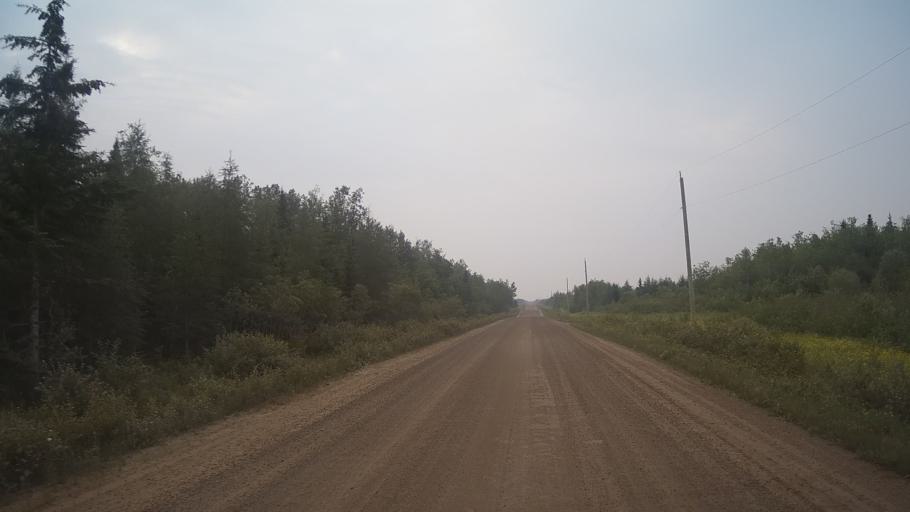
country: CA
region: Ontario
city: Hearst
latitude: 49.6376
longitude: -83.2783
